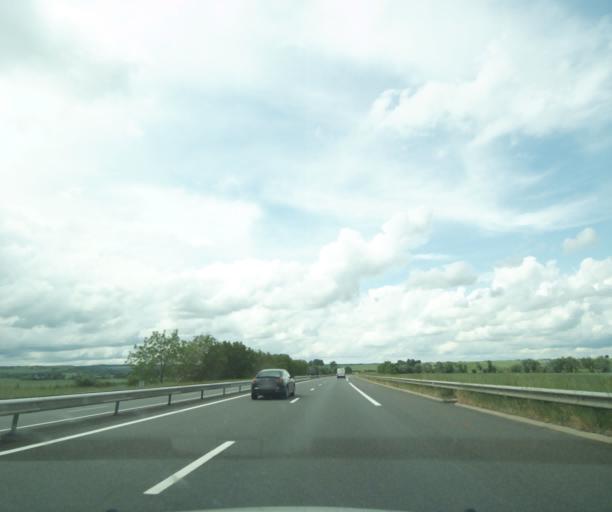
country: FR
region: Auvergne
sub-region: Departement de l'Allier
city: Bellenaves
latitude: 46.1840
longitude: 3.1160
